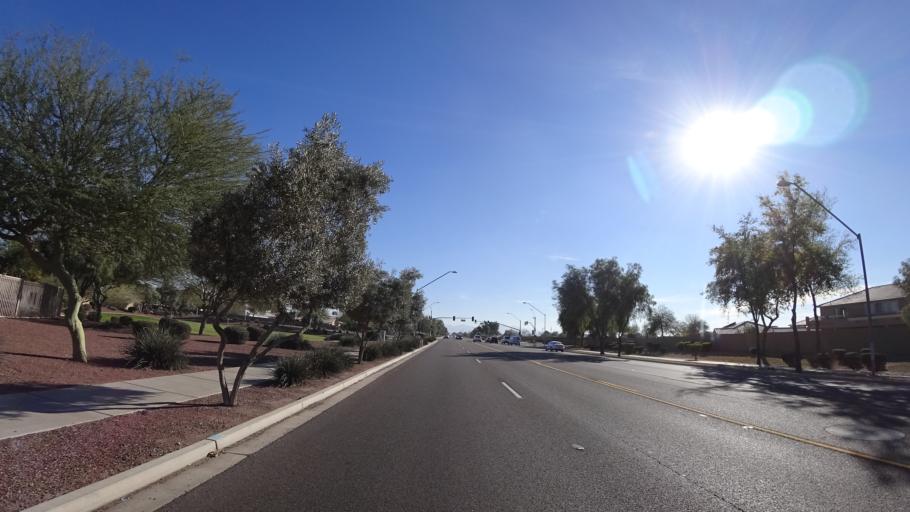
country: US
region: Arizona
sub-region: Maricopa County
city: Glendale
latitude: 33.5170
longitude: -112.2376
